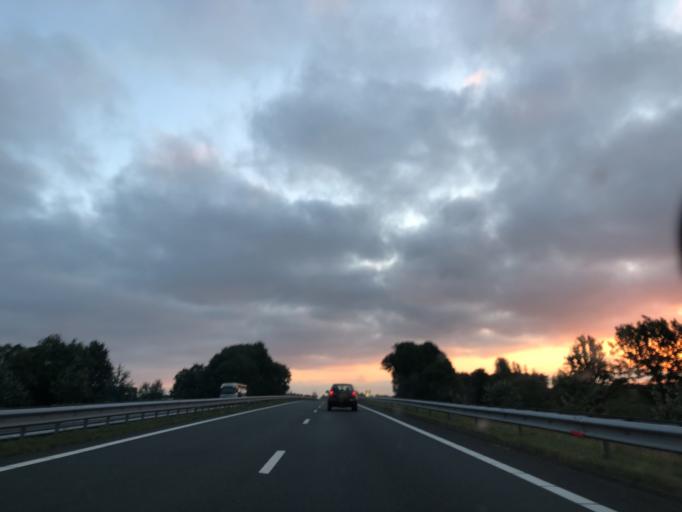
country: NL
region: Groningen
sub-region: Gemeente Veendam
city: Veendam
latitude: 53.0914
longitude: 6.8909
